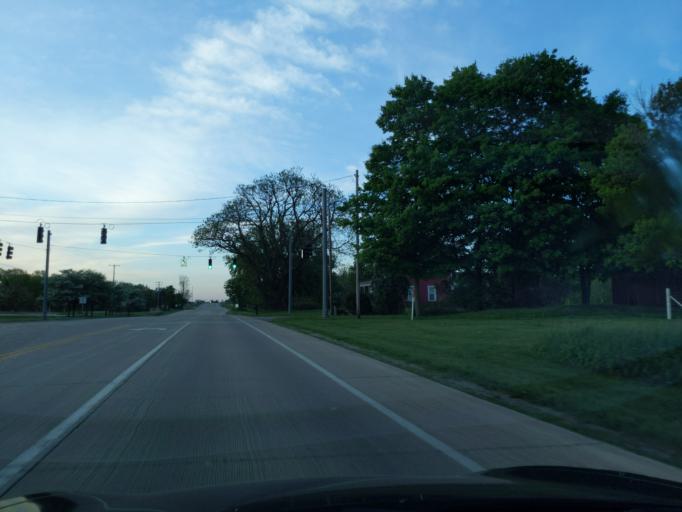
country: US
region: Michigan
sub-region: Ingham County
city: Okemos
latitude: 42.6726
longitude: -84.4328
